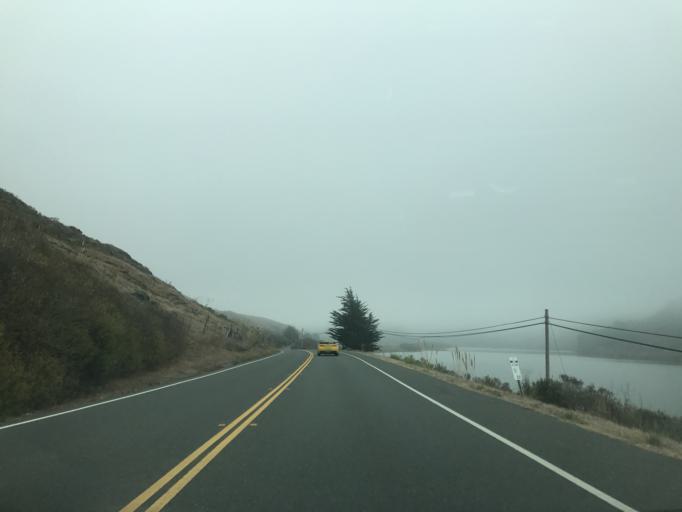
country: US
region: California
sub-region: Sonoma County
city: Monte Rio
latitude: 38.4468
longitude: -123.1129
